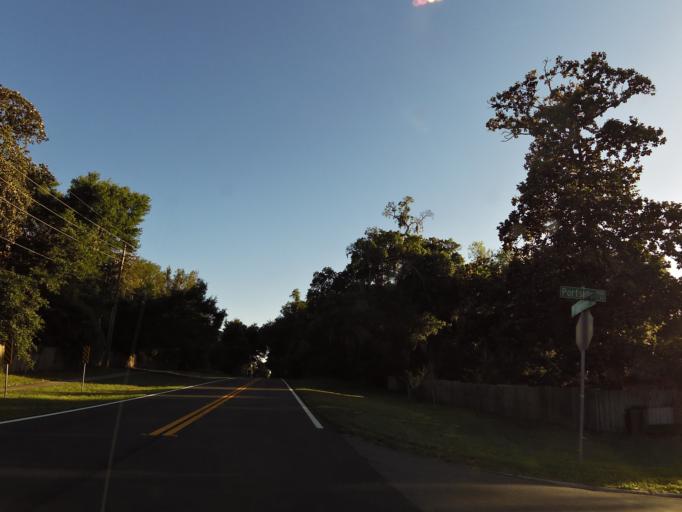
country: US
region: Florida
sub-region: Duval County
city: Atlantic Beach
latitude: 30.3767
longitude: -81.5113
